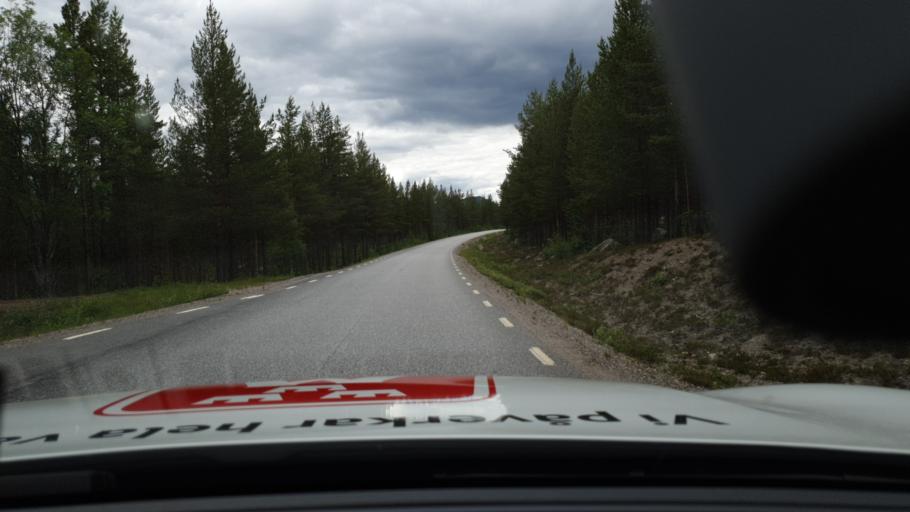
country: SE
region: Norrbotten
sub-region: Arjeplogs Kommun
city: Arjeplog
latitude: 66.9054
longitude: 18.4440
